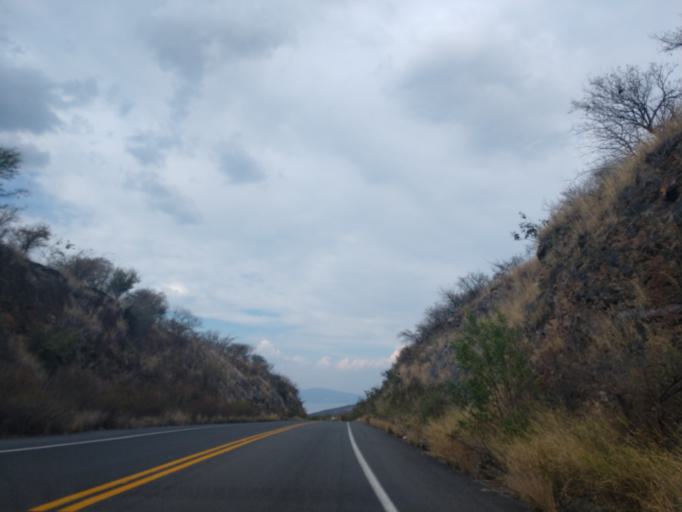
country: MX
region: Jalisco
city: La Manzanilla de la Paz
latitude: 20.1131
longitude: -103.1656
